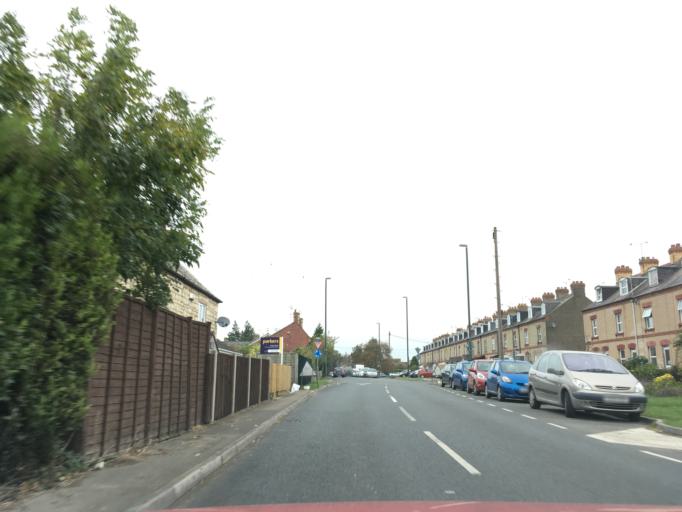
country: GB
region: England
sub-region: Gloucestershire
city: Stonehouse
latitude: 51.7528
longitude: -2.2828
